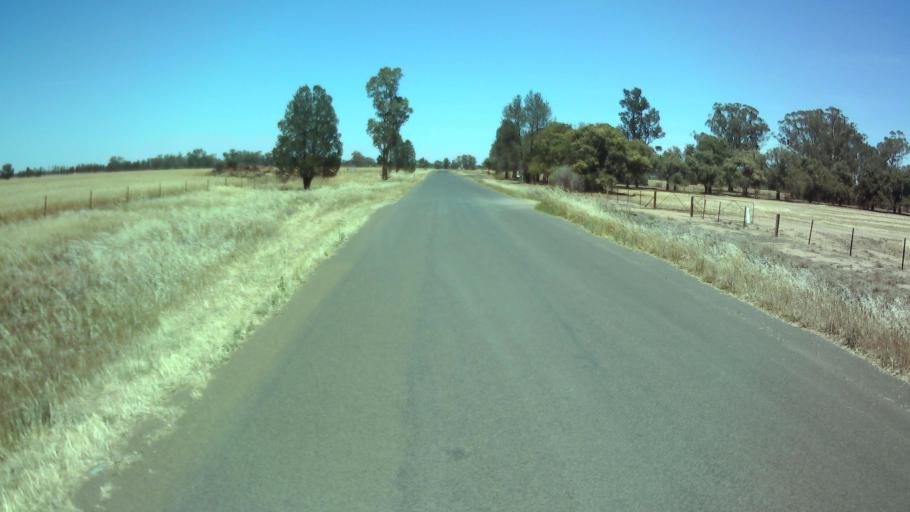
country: AU
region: New South Wales
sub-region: Weddin
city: Grenfell
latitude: -34.0308
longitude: 147.7907
